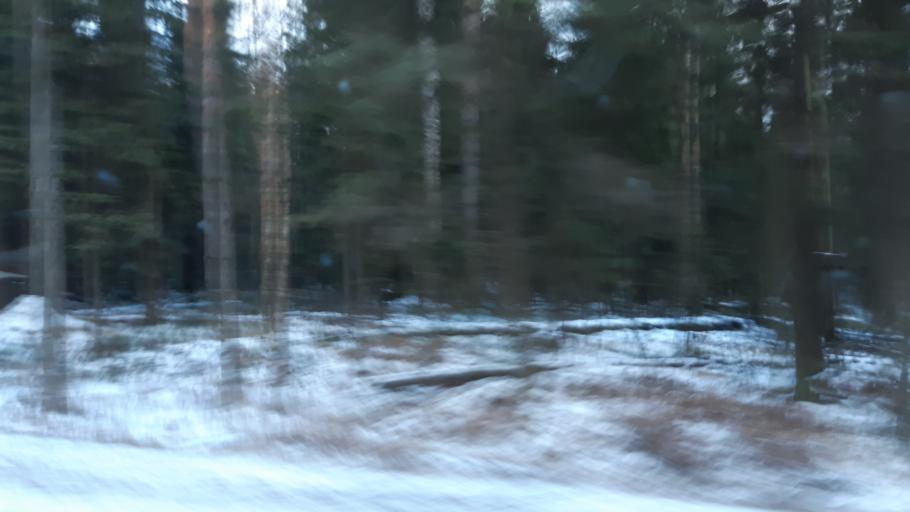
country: RU
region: Moskovskaya
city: Noginsk-9
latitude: 55.9628
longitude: 38.5419
